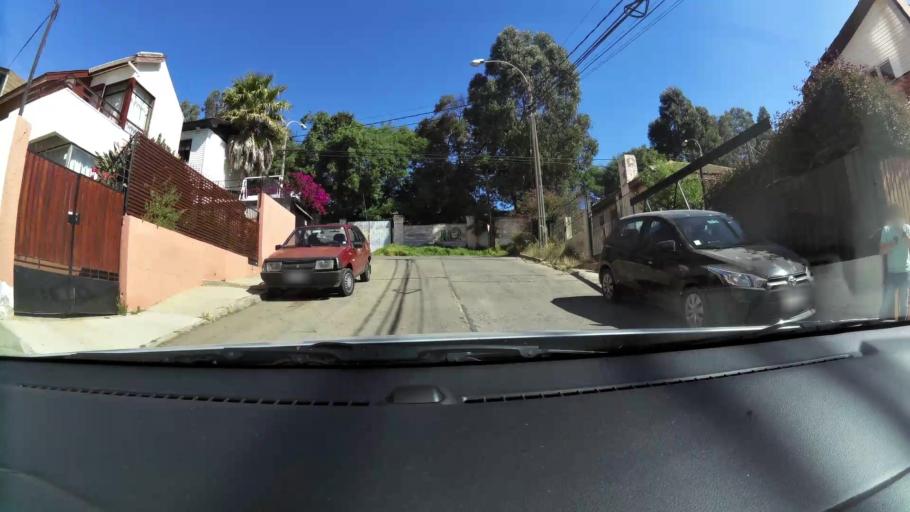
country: CL
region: Valparaiso
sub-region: Provincia de Valparaiso
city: Vina del Mar
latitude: -33.0313
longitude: -71.5724
